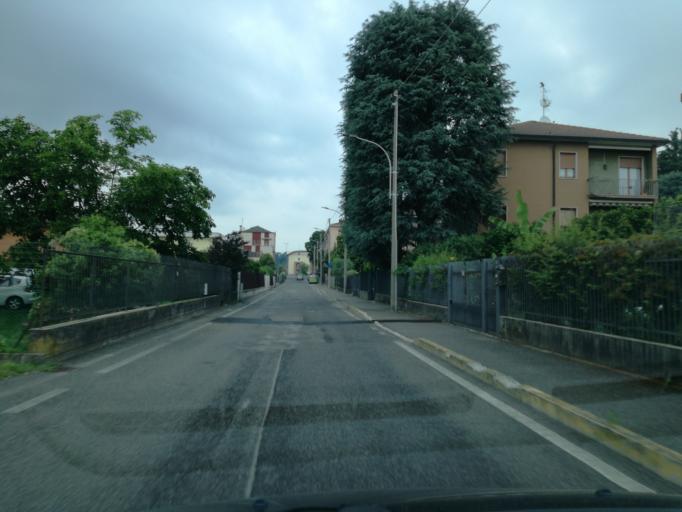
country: IT
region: Lombardy
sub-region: Provincia di Monza e Brianza
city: Carnate
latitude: 45.6505
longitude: 9.3756
